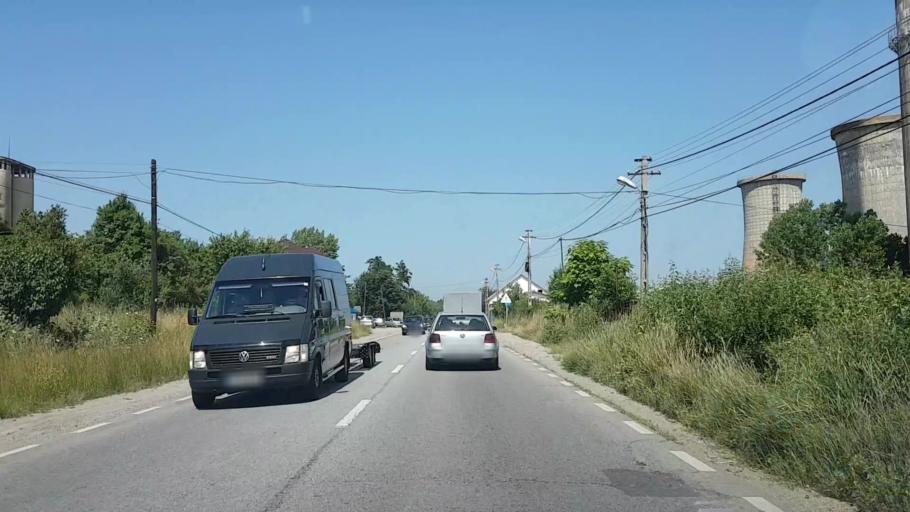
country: RO
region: Cluj
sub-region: Comuna Cusdrioara
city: Cusdrioara
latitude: 47.1627
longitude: 23.8950
